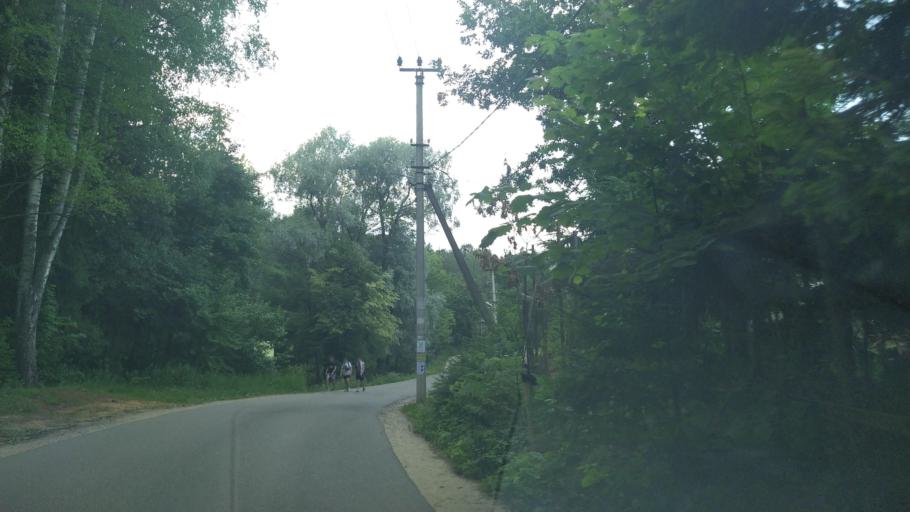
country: RU
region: Leningrad
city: Toksovo
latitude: 60.1713
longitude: 30.5308
